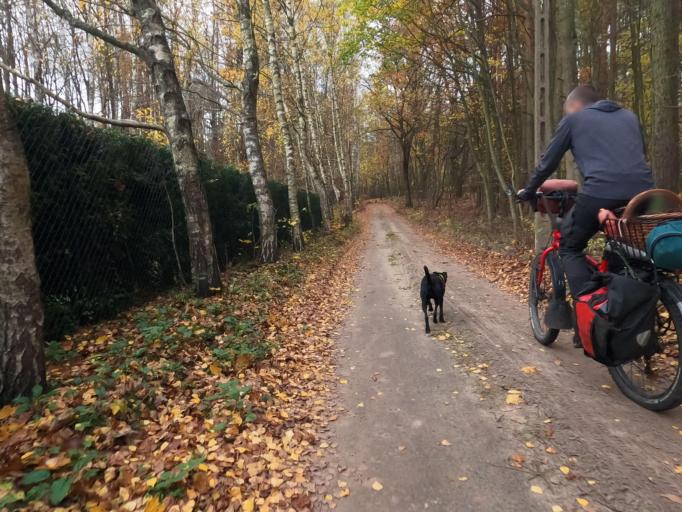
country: PL
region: Pomeranian Voivodeship
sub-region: Powiat starogardzki
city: Skarszewy
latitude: 54.0422
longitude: 18.4530
